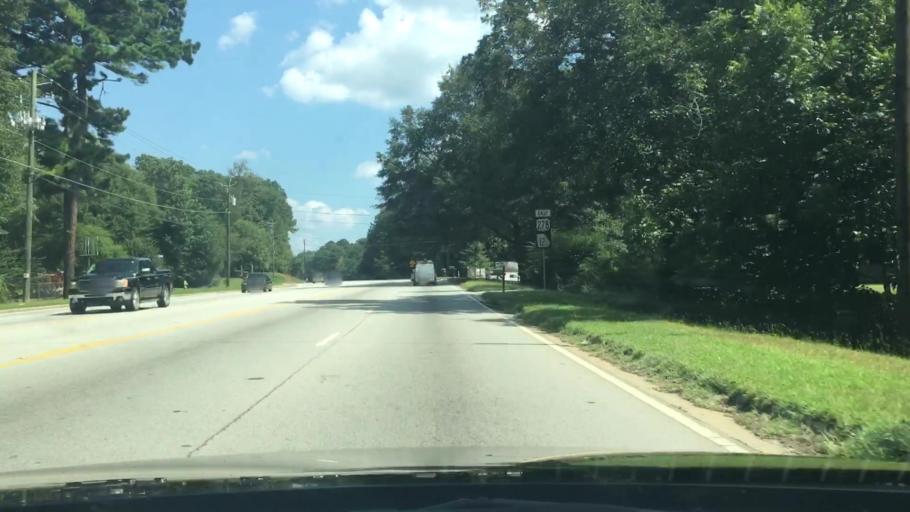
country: US
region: Georgia
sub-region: DeKalb County
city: Lithonia
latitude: 33.7127
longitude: -84.1229
